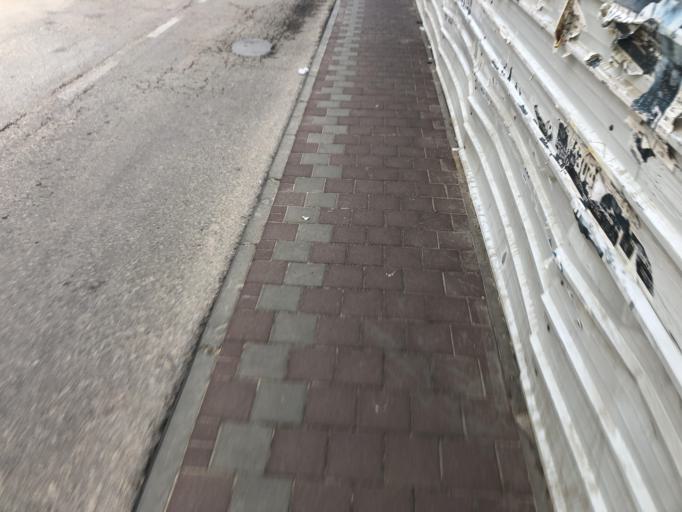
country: IL
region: Jerusalem
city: Modiin Ilit
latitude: 31.9368
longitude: 35.0455
